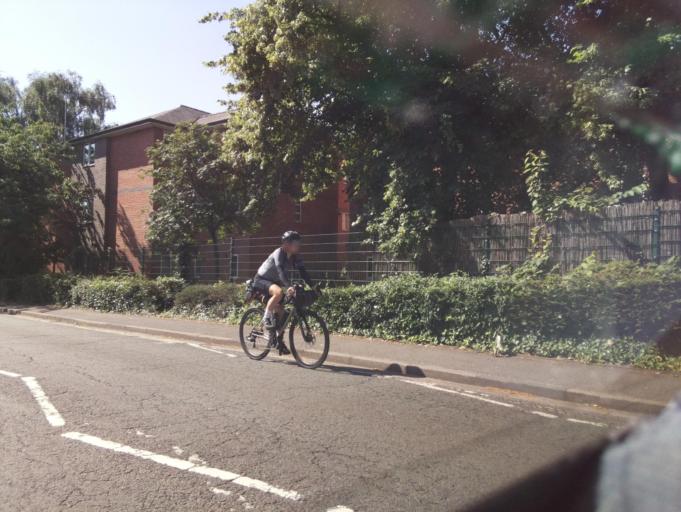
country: GB
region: England
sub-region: Derby
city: Derby
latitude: 52.9290
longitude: -1.4832
